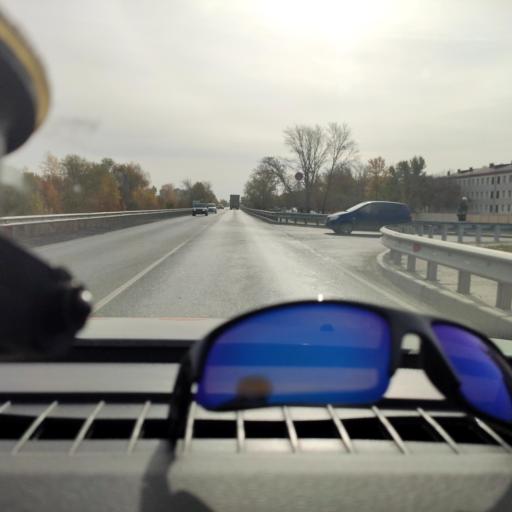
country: RU
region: Samara
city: Samara
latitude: 53.1187
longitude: 50.1215
